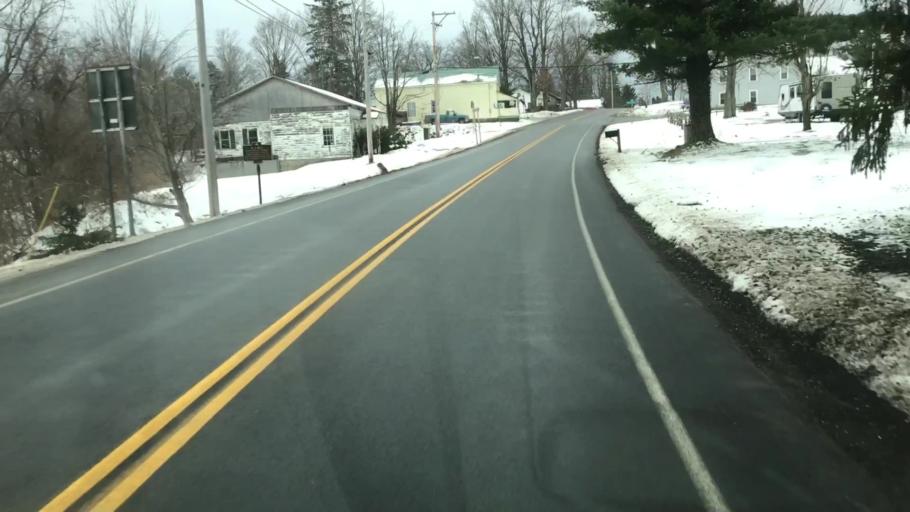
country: US
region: New York
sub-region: Cayuga County
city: Moravia
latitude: 42.7988
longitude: -76.3469
